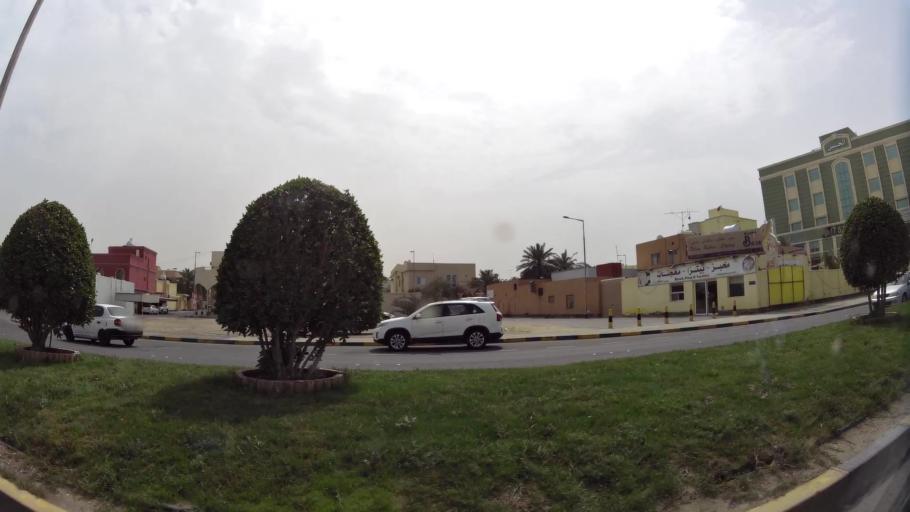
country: BH
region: Northern
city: Ar Rifa'
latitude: 26.1305
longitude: 50.5486
